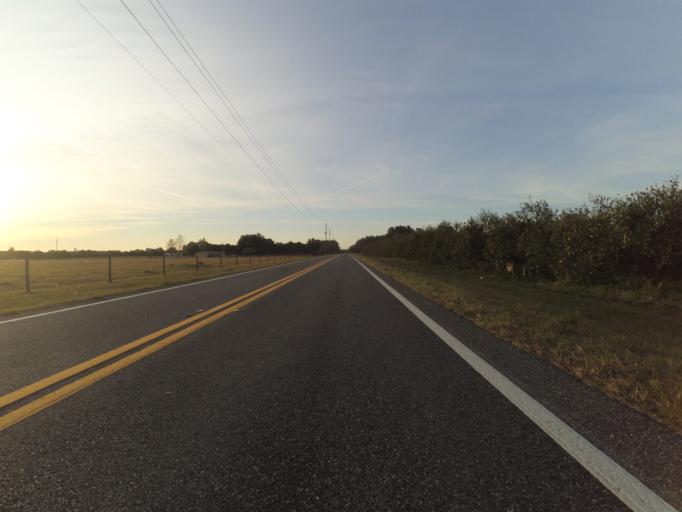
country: US
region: Florida
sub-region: Lake County
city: Umatilla
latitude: 28.9521
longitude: -81.6789
